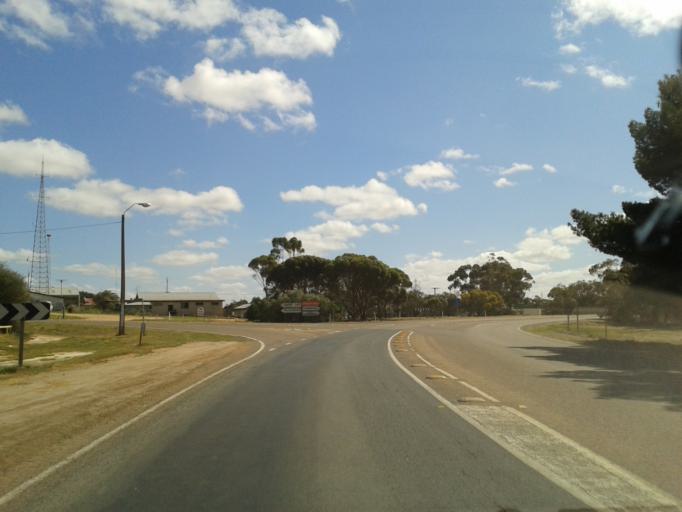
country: AU
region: South Australia
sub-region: Loxton Waikerie
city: Loxton
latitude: -35.2627
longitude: 140.9102
